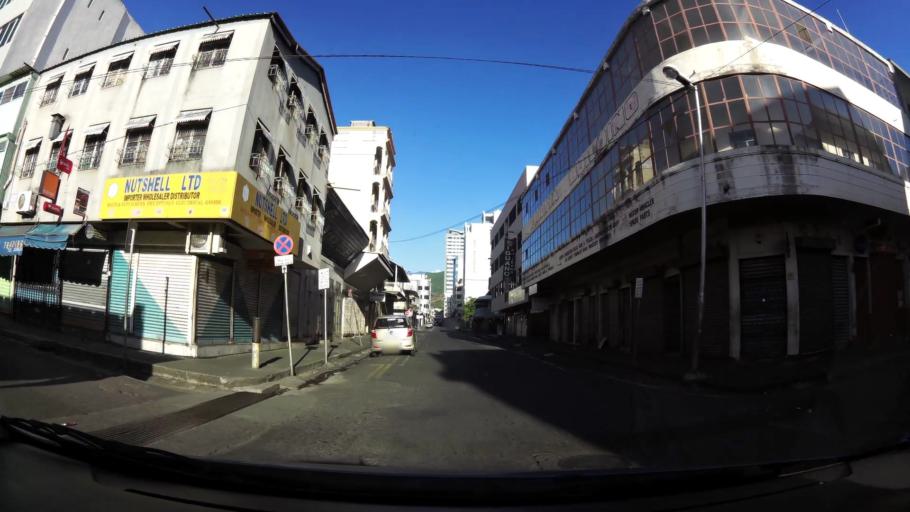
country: MU
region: Port Louis
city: Port Louis
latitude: -20.1602
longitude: 57.5042
